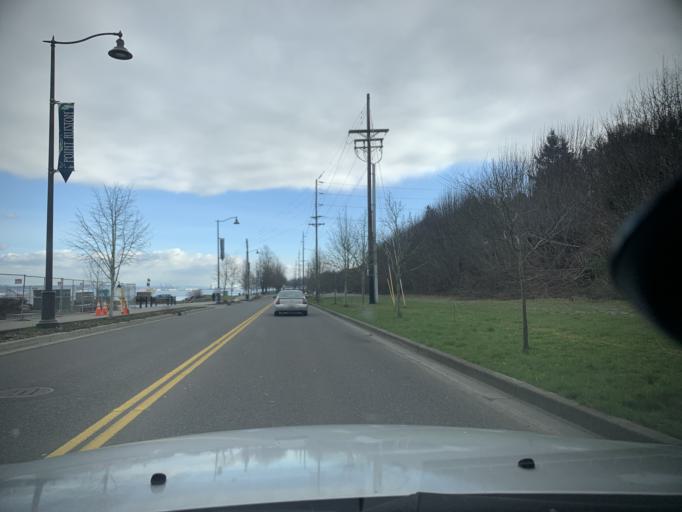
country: US
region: Washington
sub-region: Pierce County
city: Fircrest
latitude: 47.2955
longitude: -122.5010
